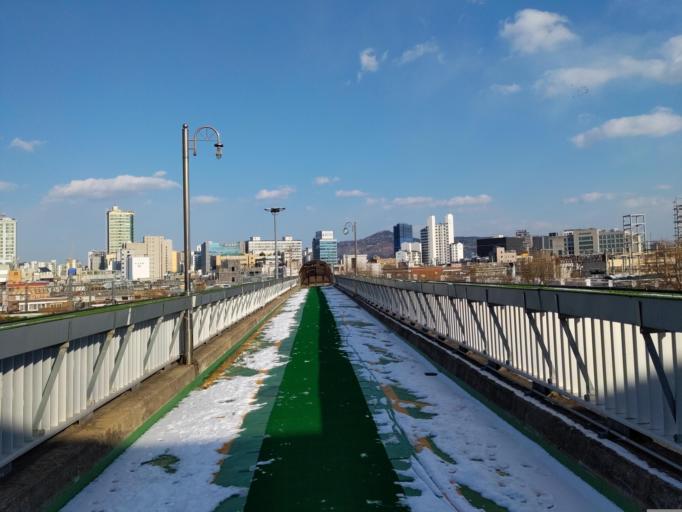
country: KR
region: Seoul
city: Seoul
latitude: 37.5624
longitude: 127.0498
